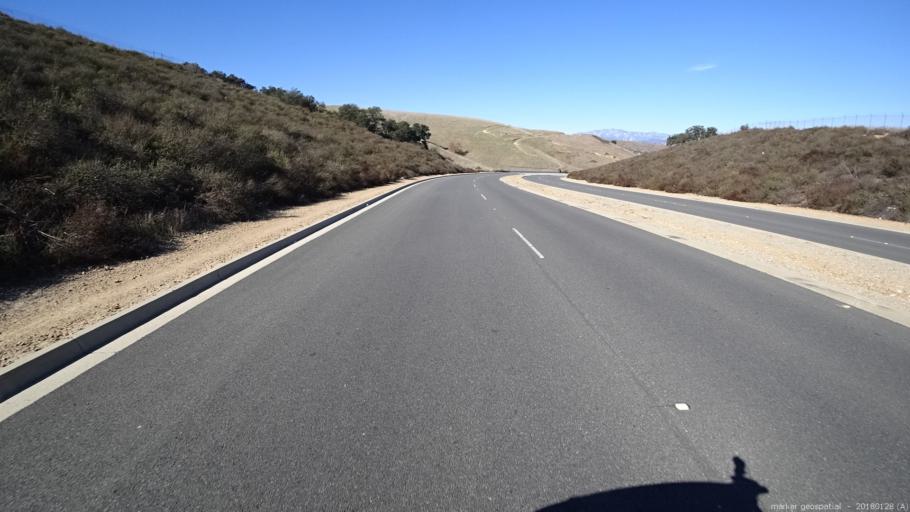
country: US
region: California
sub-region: San Bernardino County
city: Chino Hills
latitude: 34.0172
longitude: -117.7708
